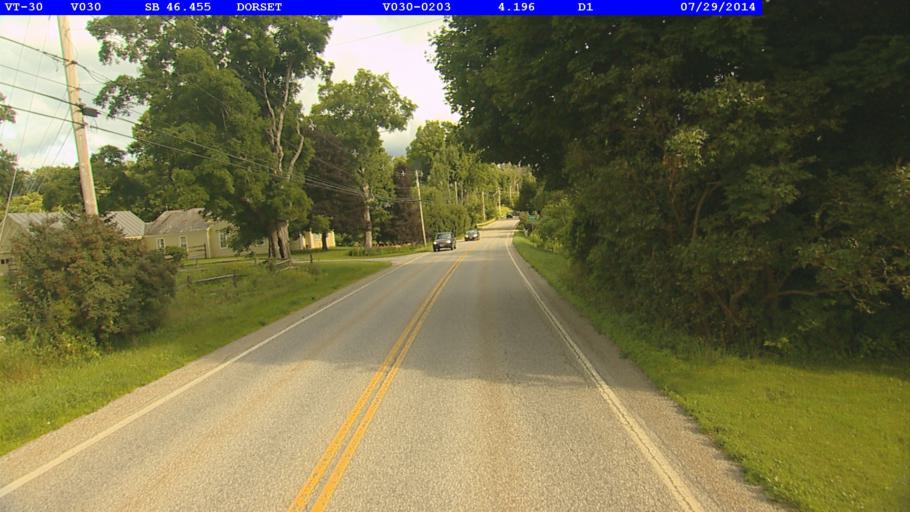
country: US
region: Vermont
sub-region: Bennington County
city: Manchester Center
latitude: 43.2653
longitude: -73.1062
